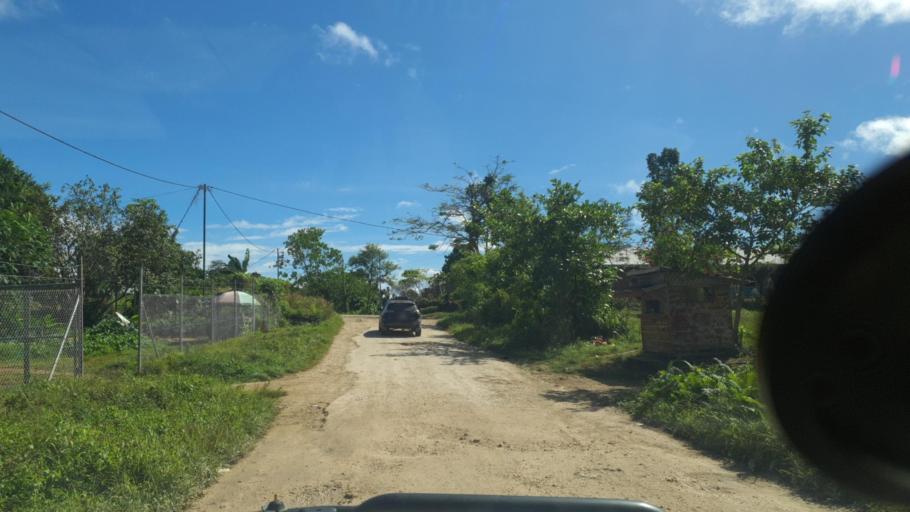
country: SB
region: Western Province
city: Gizo
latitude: -8.2469
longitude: 157.1993
